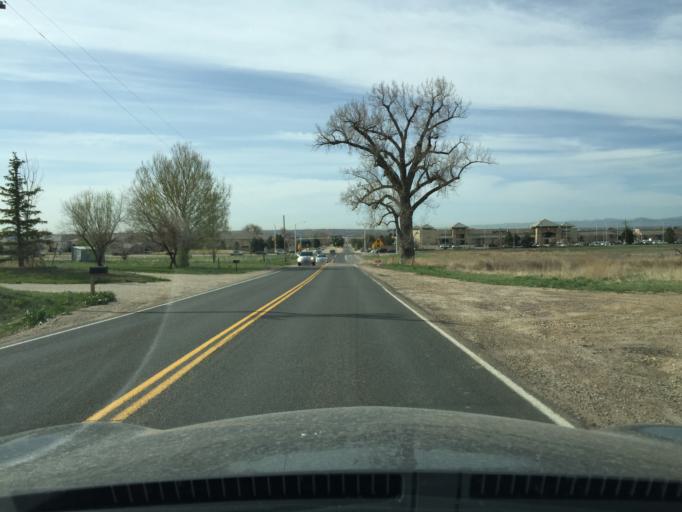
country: US
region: Colorado
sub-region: Boulder County
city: Lafayette
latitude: 39.9599
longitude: -105.0345
